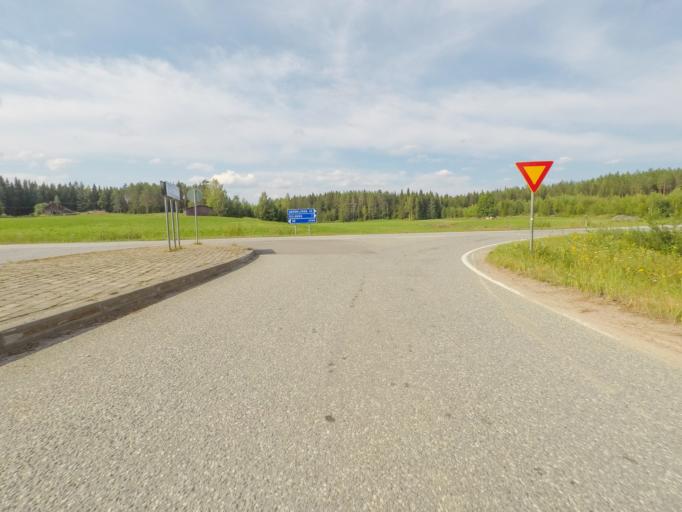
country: FI
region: Southern Savonia
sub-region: Savonlinna
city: Sulkava
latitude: 61.7903
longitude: 28.2426
